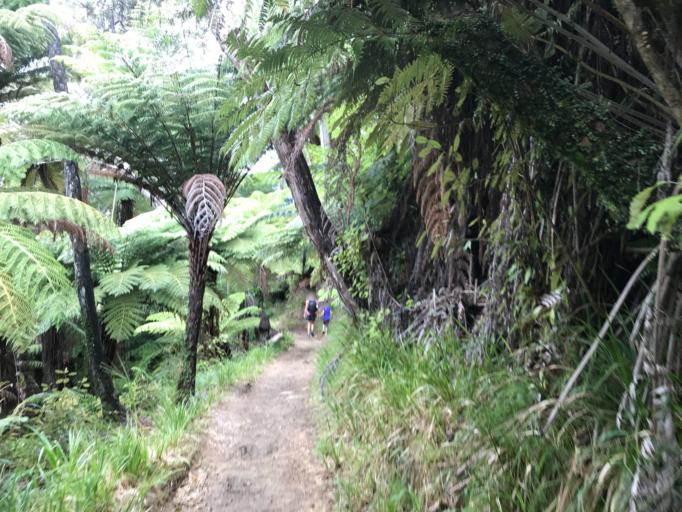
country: NZ
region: Marlborough
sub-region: Marlborough District
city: Picton
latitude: -41.2516
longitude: 173.9522
